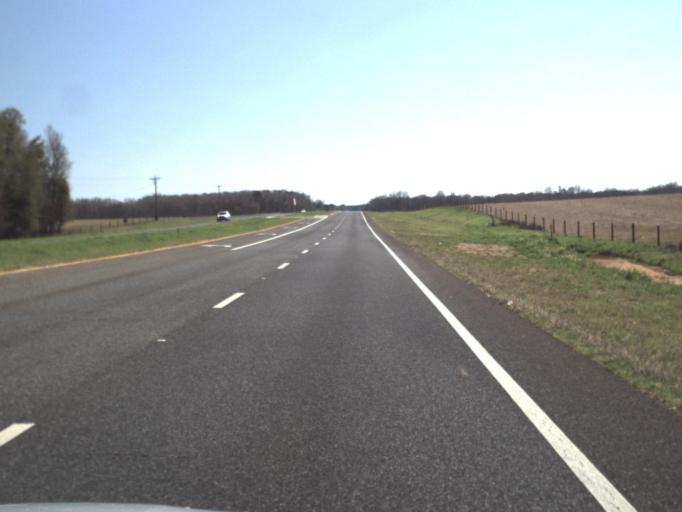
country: US
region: Florida
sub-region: Jackson County
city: Marianna
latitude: 30.8652
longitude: -85.3576
